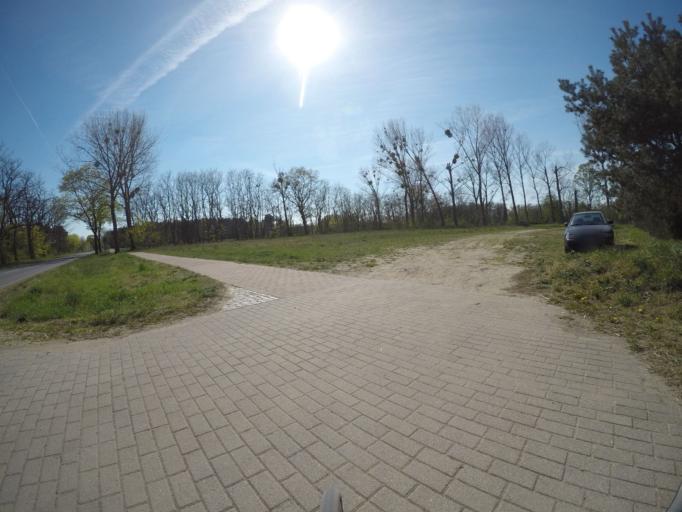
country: DE
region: Brandenburg
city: Rehfelde
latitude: 52.4968
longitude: 13.9200
